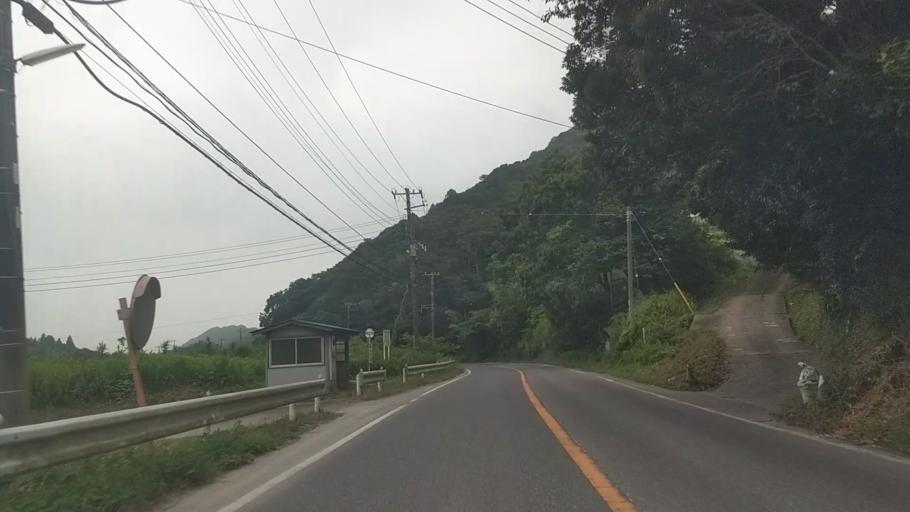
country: JP
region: Chiba
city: Tateyama
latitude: 35.1443
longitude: 139.8676
